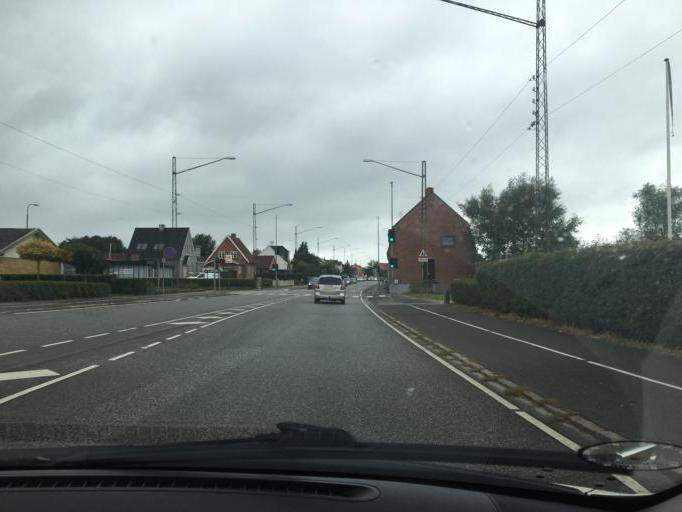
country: DK
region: South Denmark
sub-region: Middelfart Kommune
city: Middelfart
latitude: 55.4985
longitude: 9.7442
